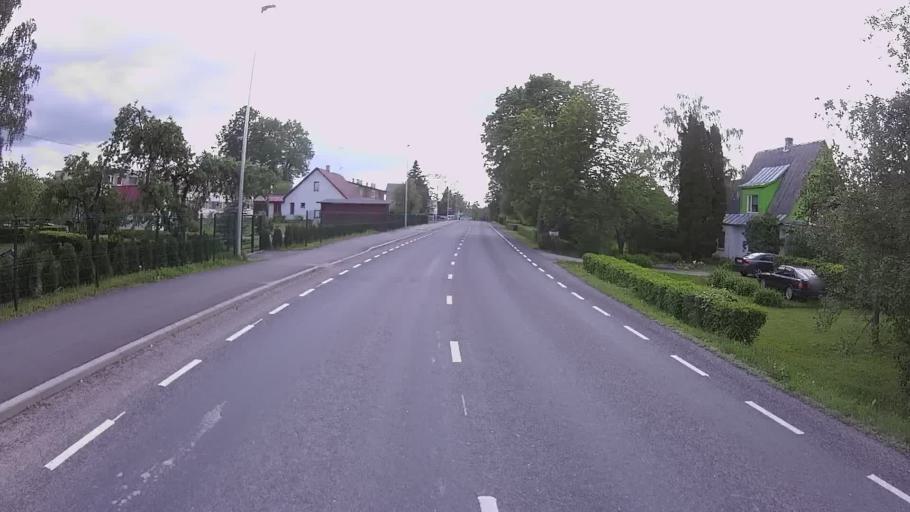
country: EE
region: Jogevamaa
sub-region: Mustvee linn
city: Mustvee
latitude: 58.9868
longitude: 26.8725
